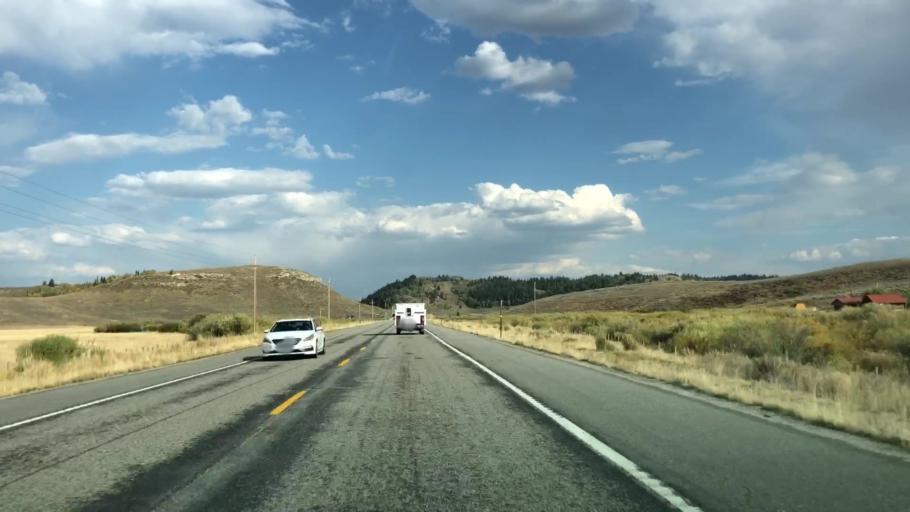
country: US
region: Wyoming
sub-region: Teton County
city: Hoback
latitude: 43.1568
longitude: -110.3526
